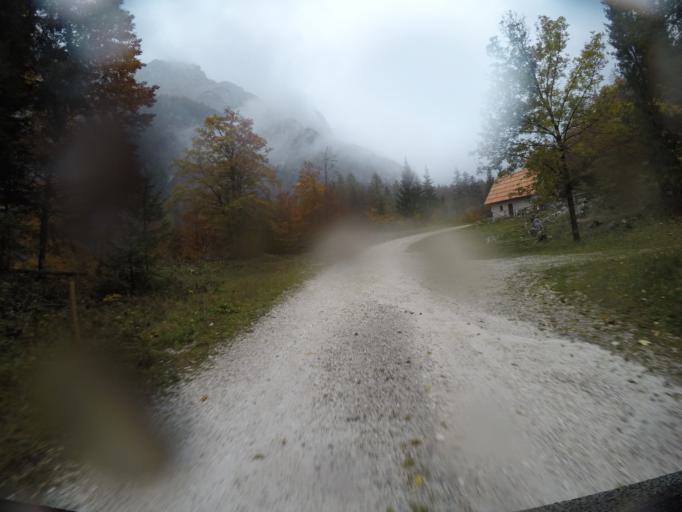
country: SI
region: Kranjska Gora
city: Kranjska Gora
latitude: 46.4051
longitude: 13.7140
